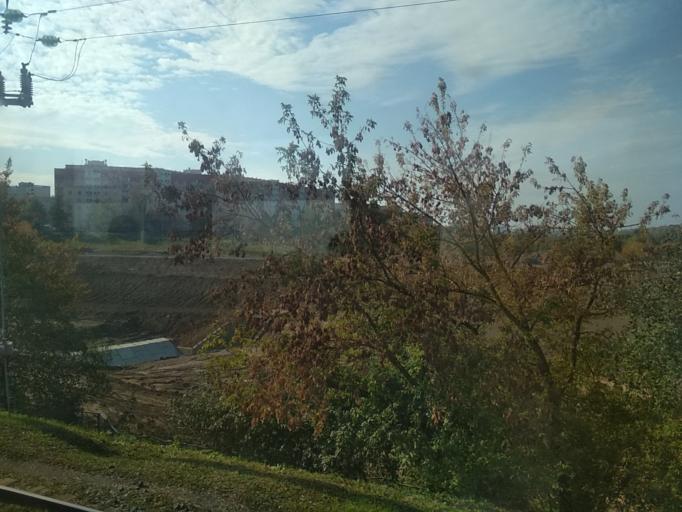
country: BY
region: Minsk
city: Syenitsa
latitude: 53.8559
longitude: 27.5578
